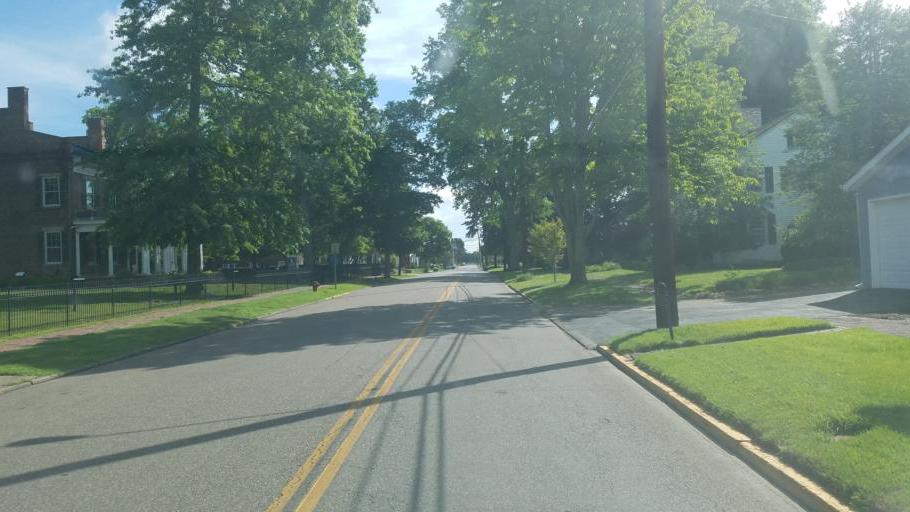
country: US
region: Ohio
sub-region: Gallia County
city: Gallipolis
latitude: 38.8088
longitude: -82.2017
